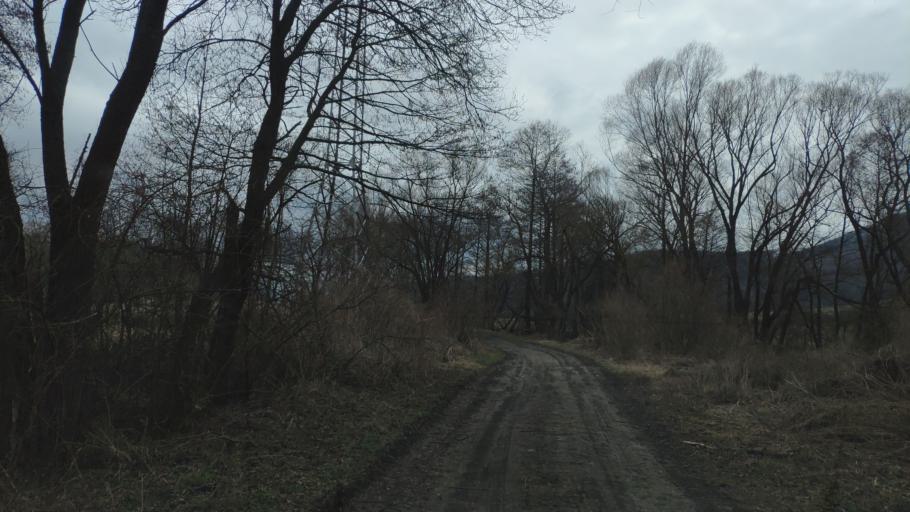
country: SK
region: Presovsky
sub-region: Okres Presov
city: Presov
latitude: 49.0761
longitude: 21.2948
